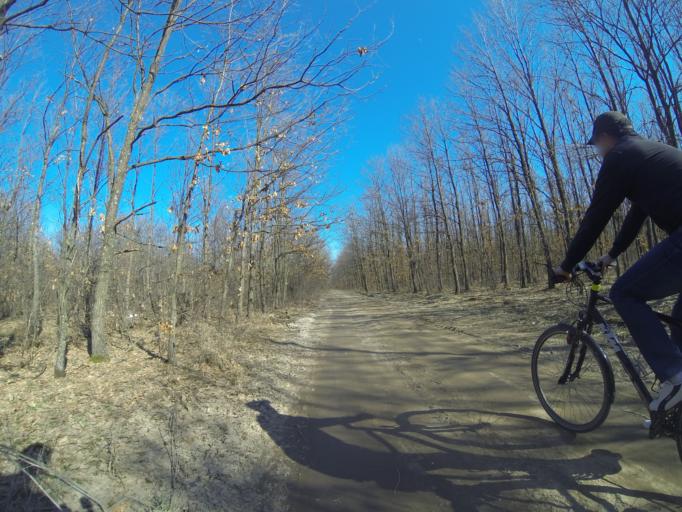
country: RO
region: Dolj
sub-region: Comuna Tuglui
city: Tuglui
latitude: 44.1433
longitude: 23.8170
